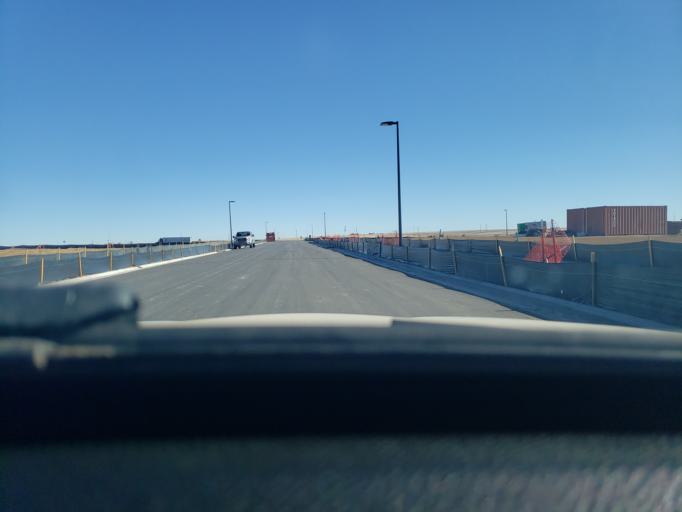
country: US
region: Colorado
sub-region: Adams County
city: Aurora
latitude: 39.7748
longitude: -104.7049
